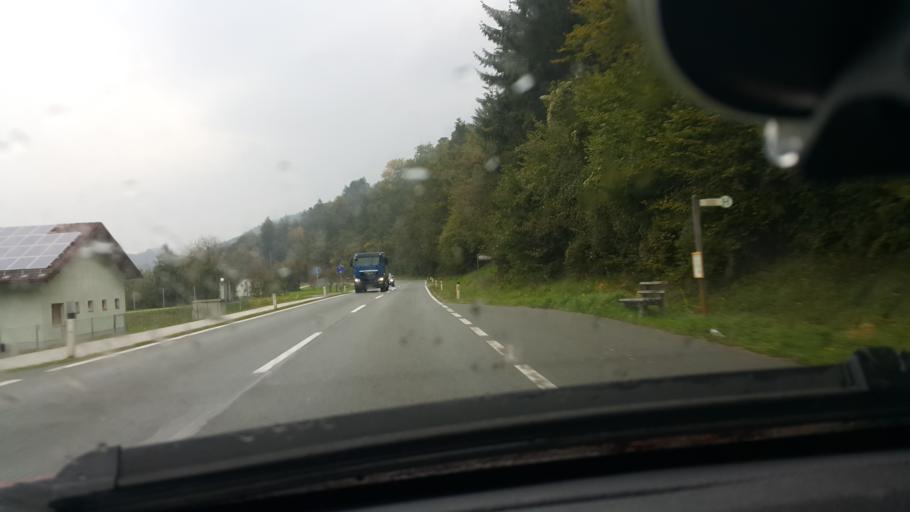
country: AT
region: Carinthia
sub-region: Politischer Bezirk Wolfsberg
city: Lavamund
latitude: 46.6172
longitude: 14.9754
